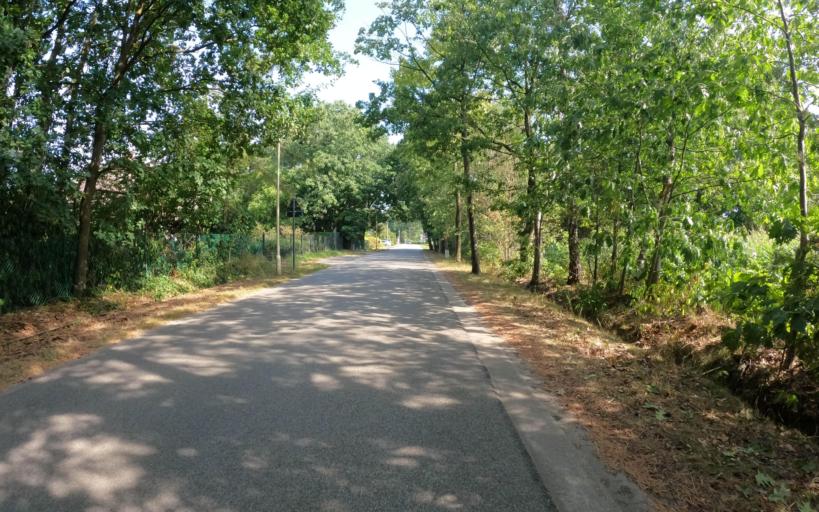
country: BE
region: Flanders
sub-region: Provincie Antwerpen
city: Zoersel
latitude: 51.2647
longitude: 4.7028
